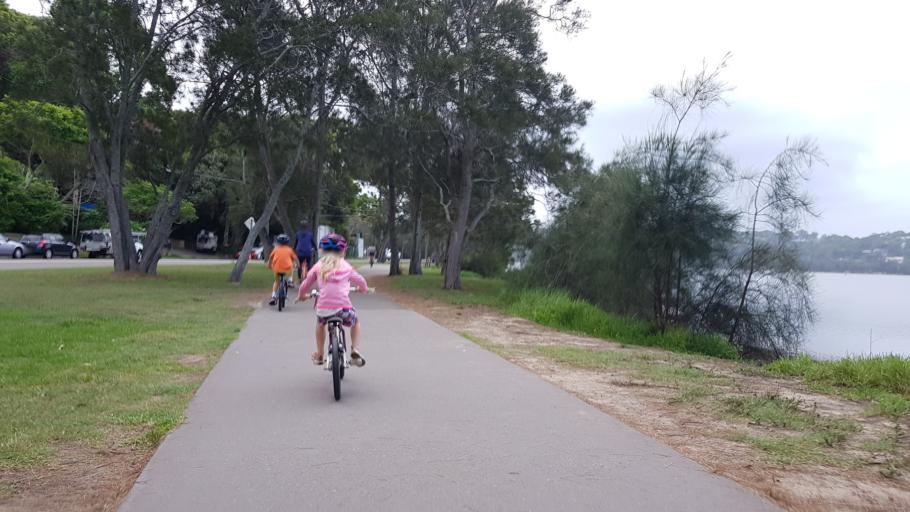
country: AU
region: New South Wales
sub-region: Warringah
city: Narrabeen
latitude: -33.7212
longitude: 151.2922
